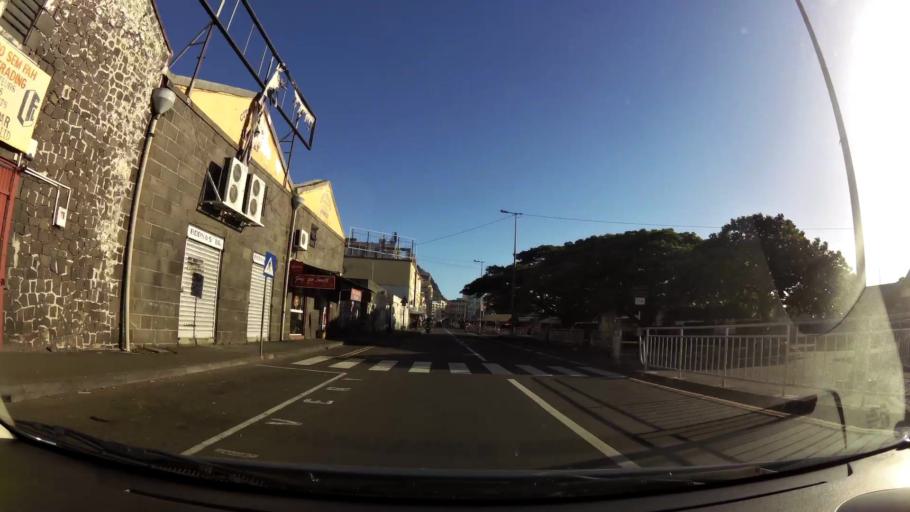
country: MU
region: Port Louis
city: Port Louis
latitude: -20.1581
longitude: 57.5053
